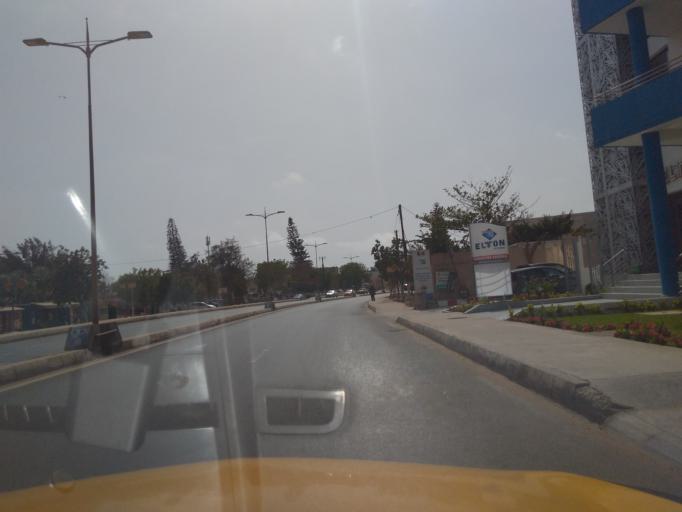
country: SN
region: Dakar
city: Mermoz Boabab
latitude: 14.7037
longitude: -17.4758
